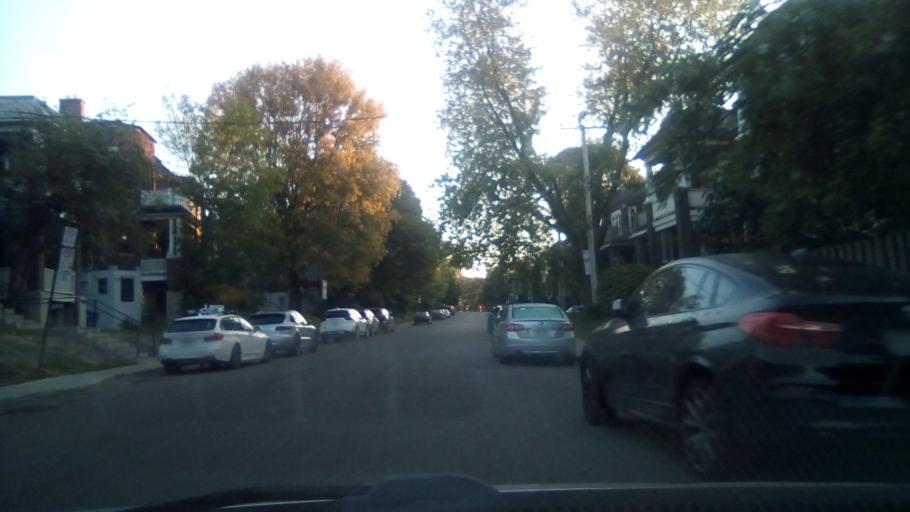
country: CA
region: Quebec
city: Saint-Raymond
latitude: 45.4786
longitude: -73.6142
